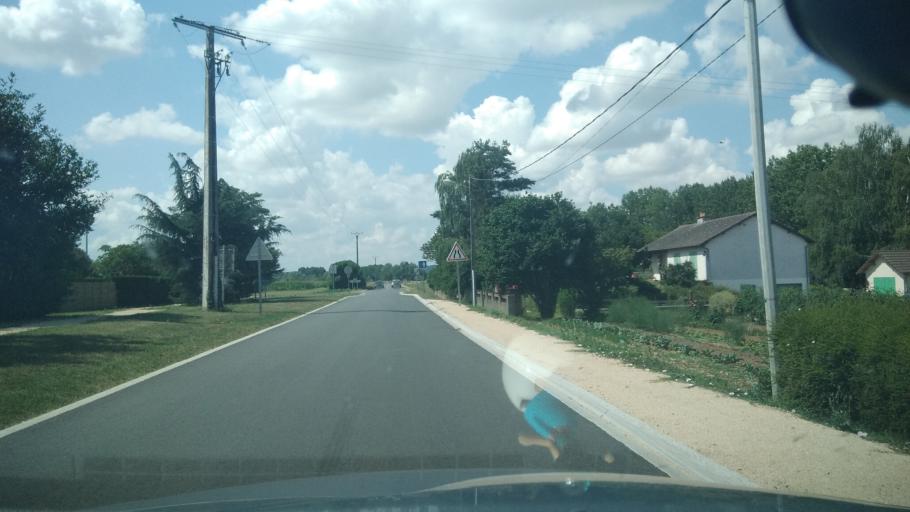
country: FR
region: Poitou-Charentes
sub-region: Departement de la Vienne
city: Dange-Saint-Romain
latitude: 46.9306
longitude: 0.5937
